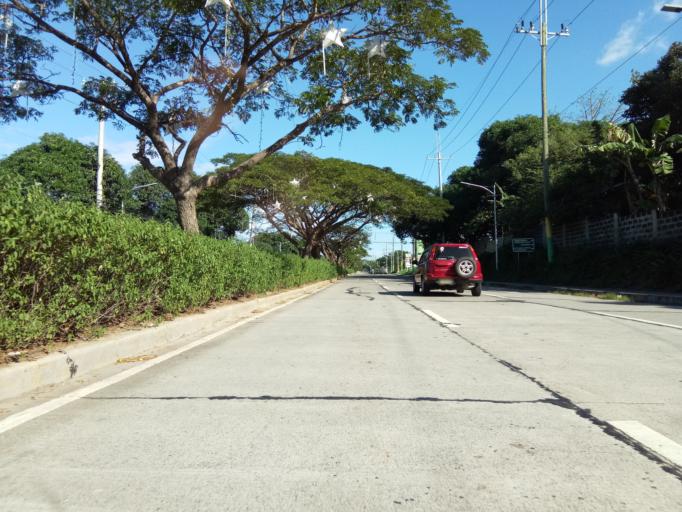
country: PH
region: Calabarzon
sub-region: Province of Cavite
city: Dasmarinas
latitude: 14.3505
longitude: 120.9624
